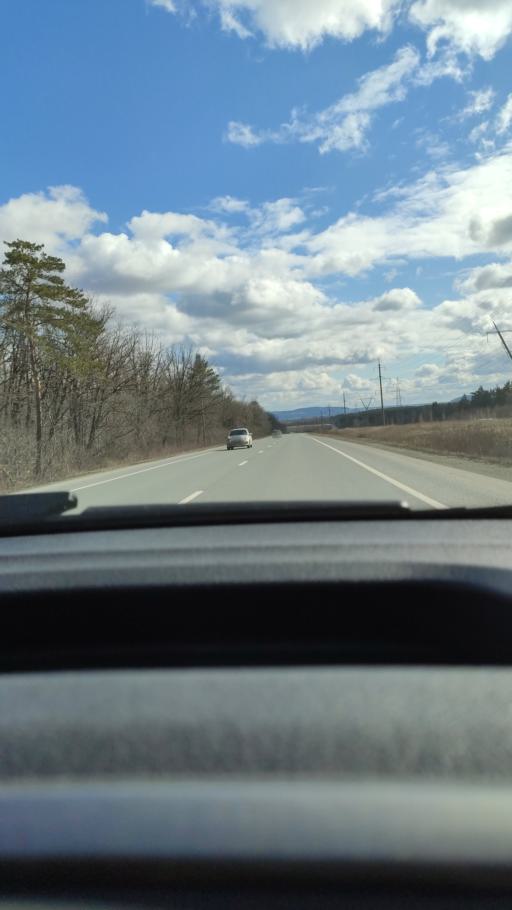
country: RU
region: Samara
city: Bogatyr'
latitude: 53.5022
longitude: 49.9482
